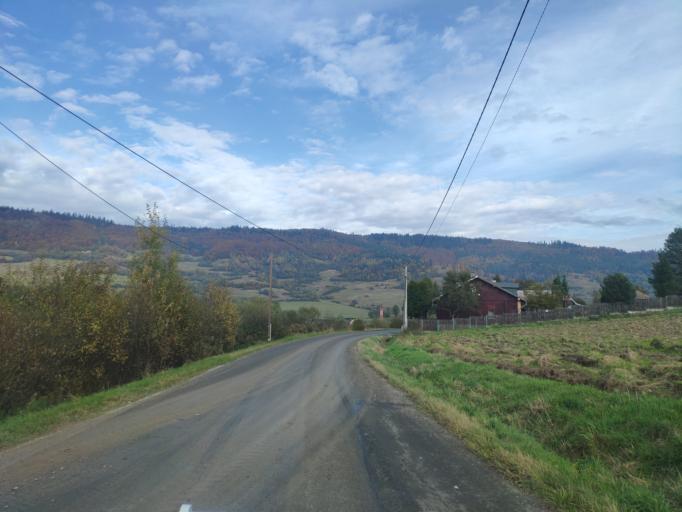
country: SK
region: Kosicky
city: Spisska Nova Ves
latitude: 48.8333
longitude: 20.6362
